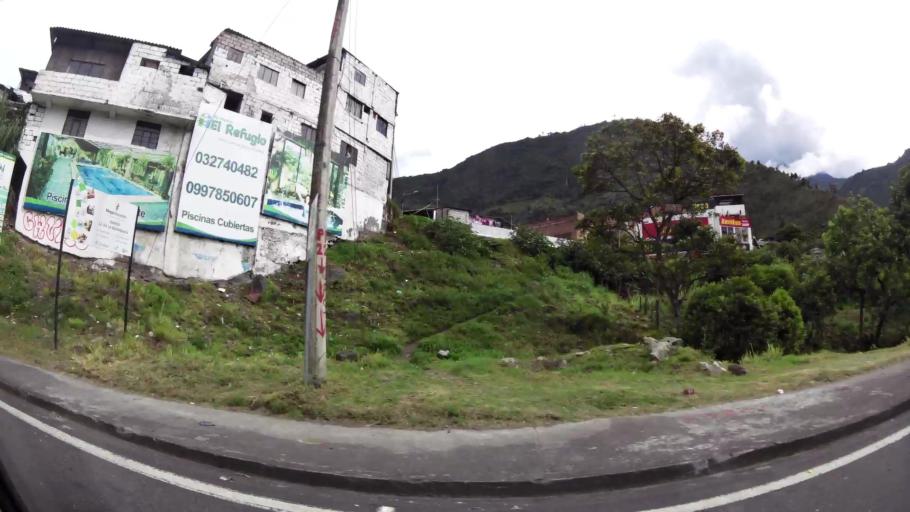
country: EC
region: Tungurahua
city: Banos
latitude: -1.3967
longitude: -78.4279
